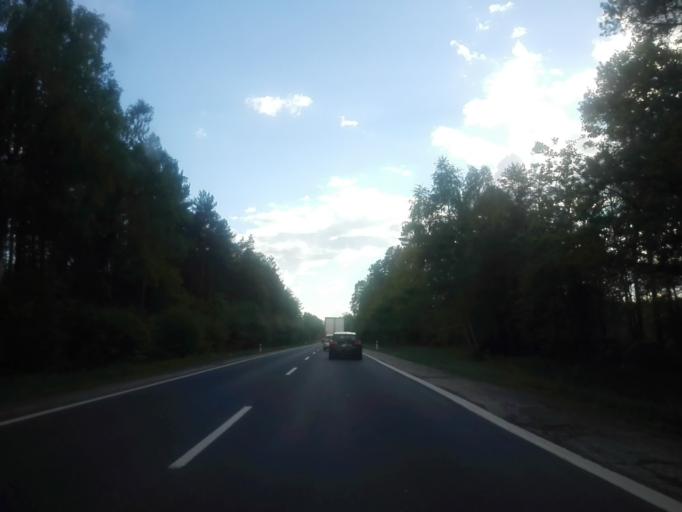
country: PL
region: Masovian Voivodeship
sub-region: Powiat wyszkowski
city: Branszczyk
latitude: 52.6869
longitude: 21.6372
